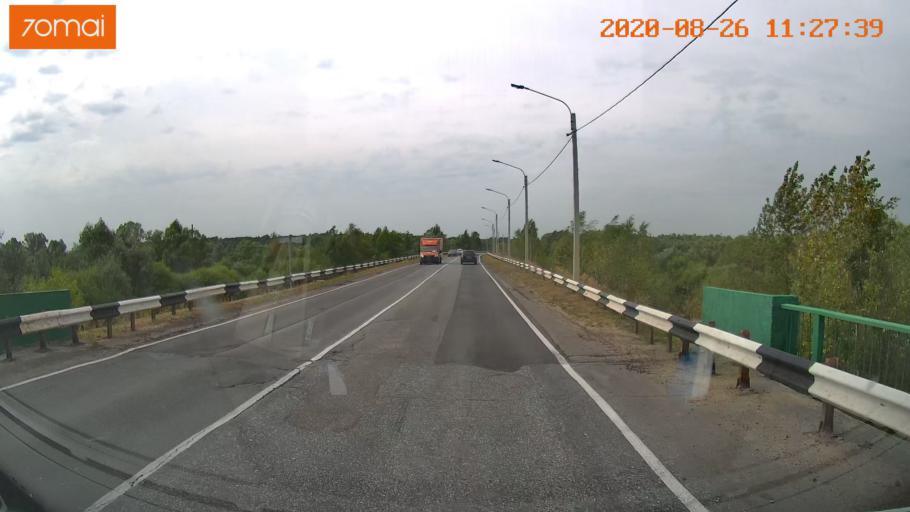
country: RU
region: Rjazan
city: Shilovo
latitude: 54.3251
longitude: 40.9303
